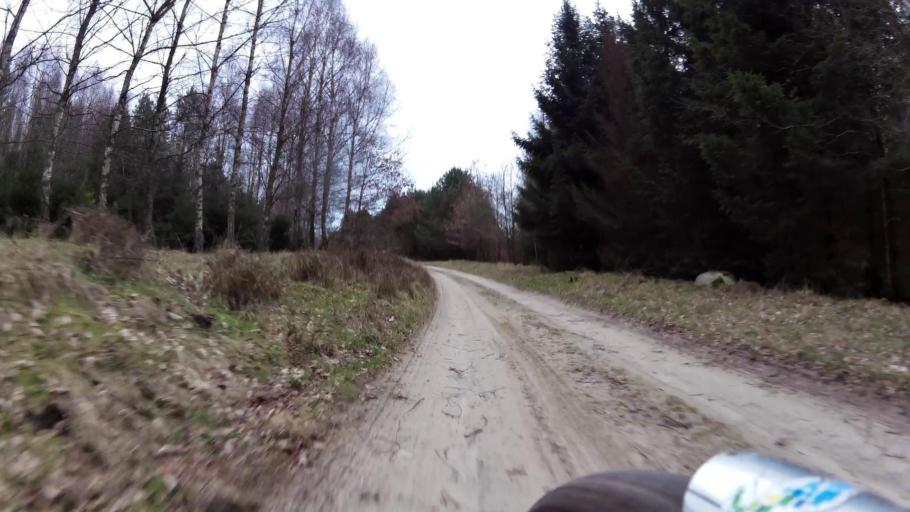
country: PL
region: Pomeranian Voivodeship
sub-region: Powiat bytowski
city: Trzebielino
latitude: 54.1152
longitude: 17.1283
